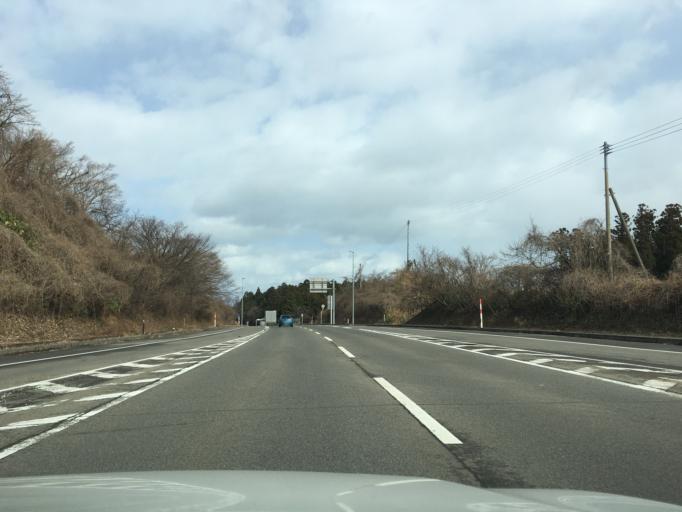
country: JP
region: Yamagata
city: Yuza
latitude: 39.2592
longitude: 139.9263
